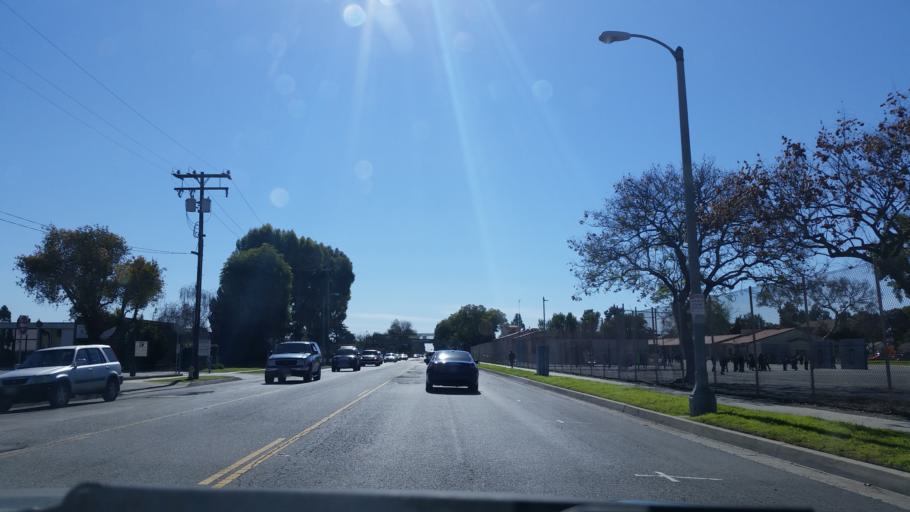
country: US
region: California
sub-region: Los Angeles County
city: Lakewood
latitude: 33.8425
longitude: -118.1338
